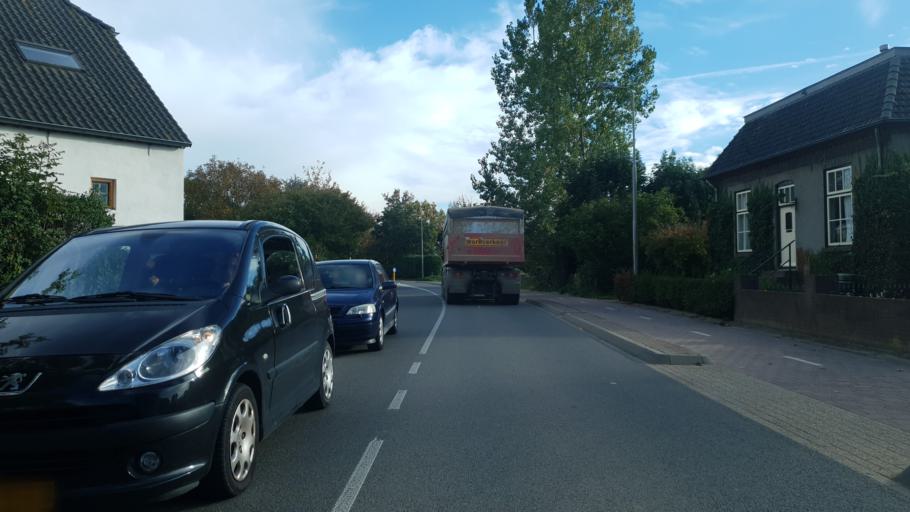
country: DE
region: North Rhine-Westphalia
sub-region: Regierungsbezirk Dusseldorf
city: Kranenburg
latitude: 51.8612
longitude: 6.0188
